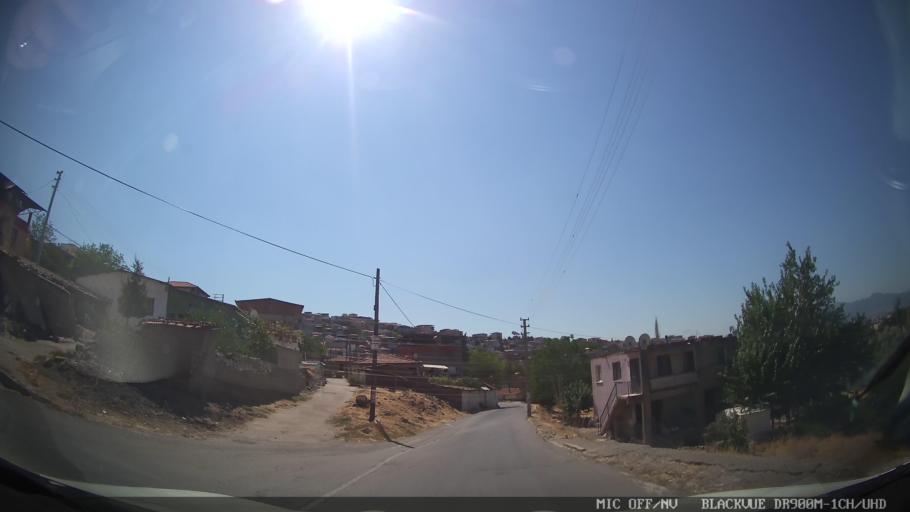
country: TR
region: Izmir
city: Karsiyaka
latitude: 38.5028
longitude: 27.0686
